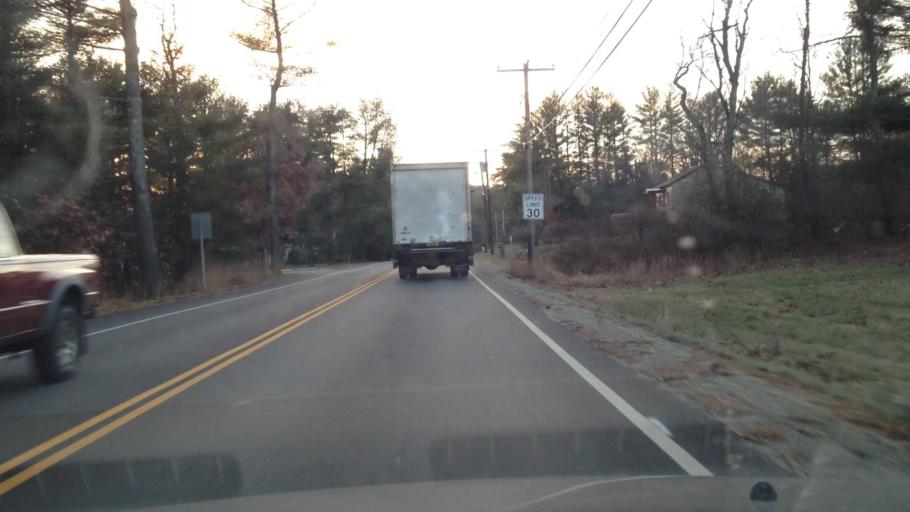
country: US
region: New Hampshire
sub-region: Cheshire County
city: Swanzey
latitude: 42.8770
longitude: -72.2739
